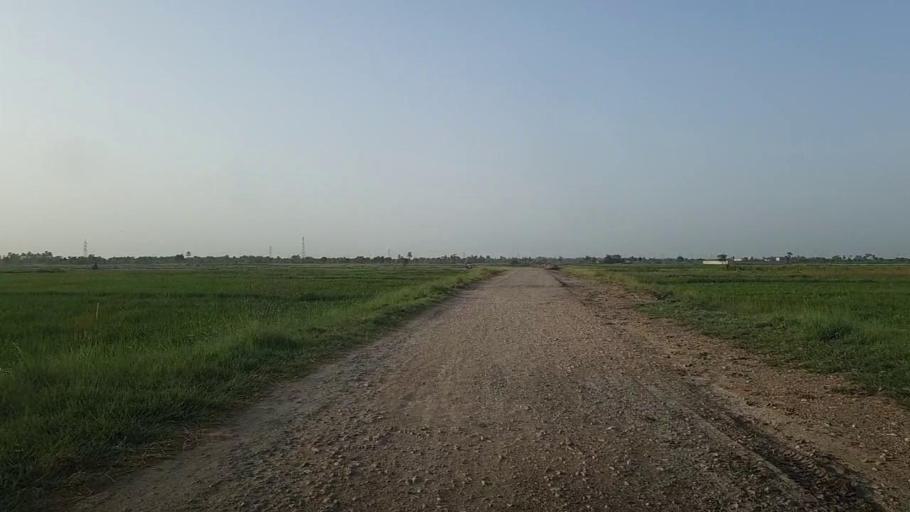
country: PK
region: Sindh
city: Naushahro Firoz
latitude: 26.8073
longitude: 68.1116
